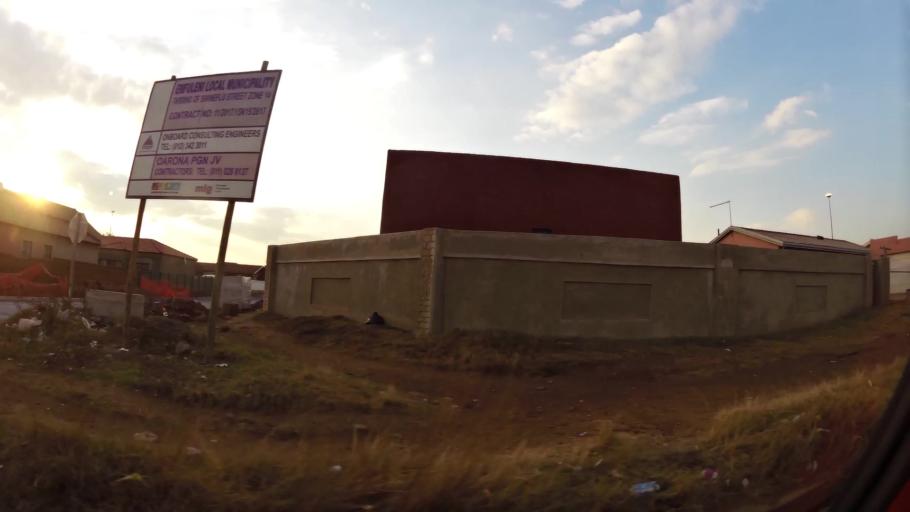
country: ZA
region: Gauteng
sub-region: City of Johannesburg Metropolitan Municipality
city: Orange Farm
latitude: -26.5933
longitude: 27.8445
